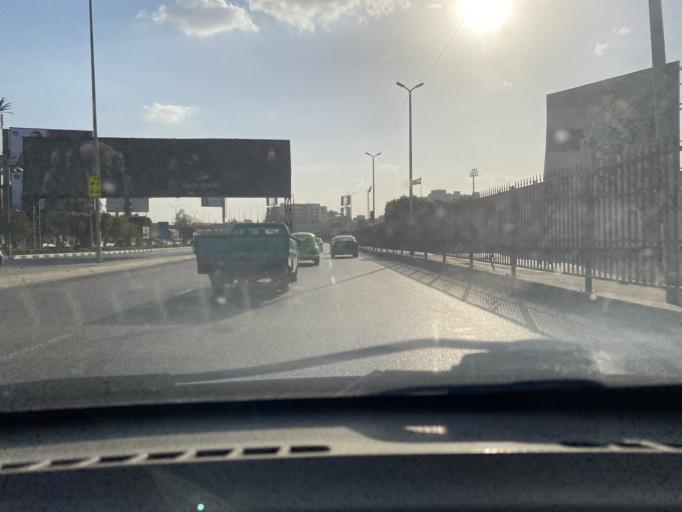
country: EG
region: Muhafazat al Qahirah
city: Cairo
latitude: 30.0718
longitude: 31.2955
